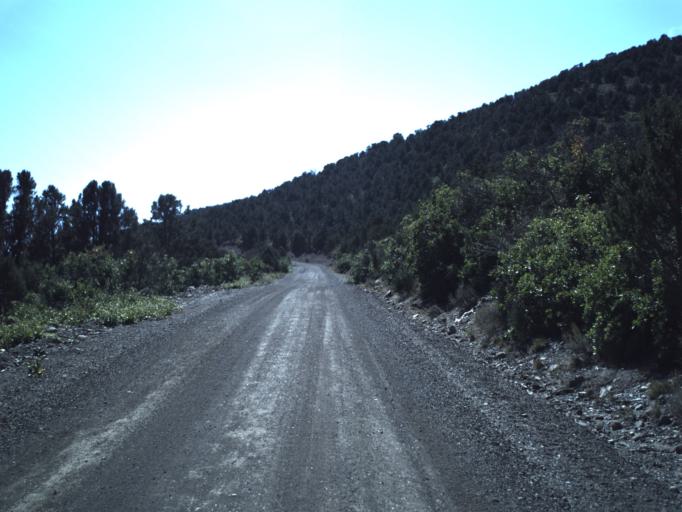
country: US
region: Utah
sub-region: Piute County
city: Junction
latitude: 38.2641
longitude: -112.3056
